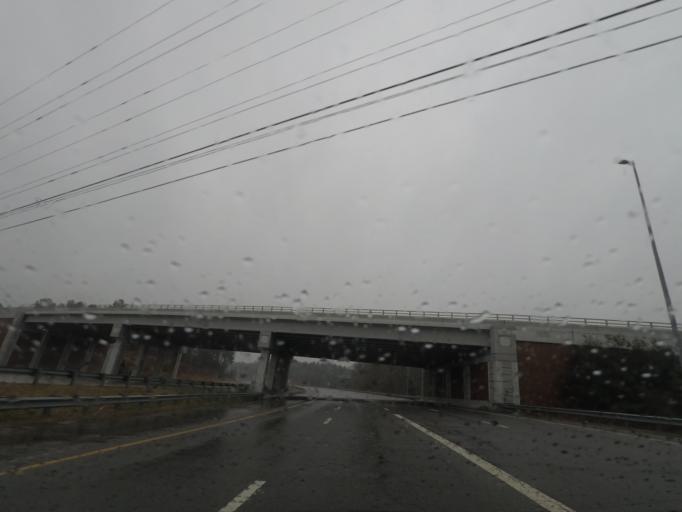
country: US
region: North Carolina
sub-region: Wake County
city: Morrisville
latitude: 35.8983
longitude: -78.8762
